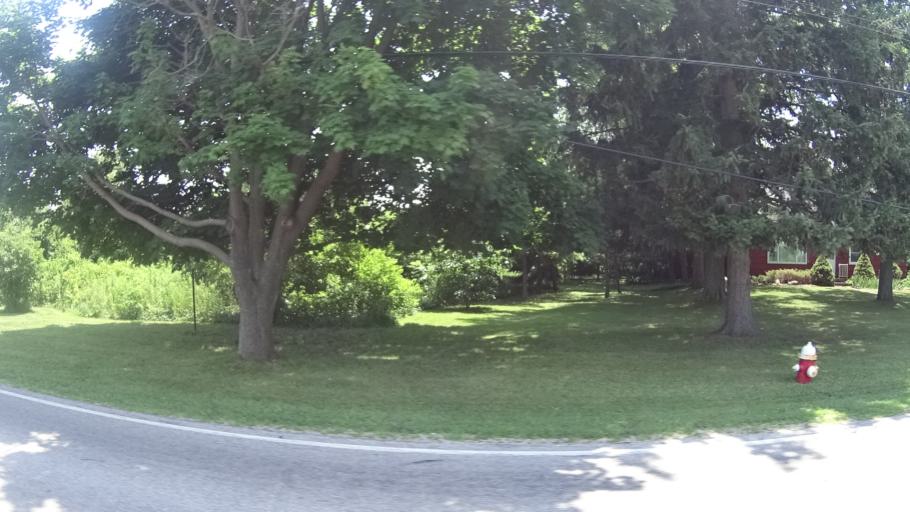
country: US
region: Ohio
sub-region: Erie County
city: Huron
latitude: 41.4118
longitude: -82.6315
